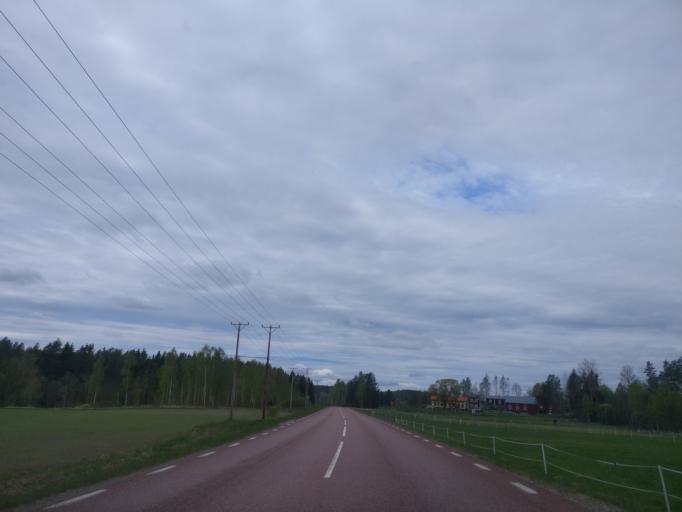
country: SE
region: Gaevleborg
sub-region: Soderhamns Kommun
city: Soderhamn
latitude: 61.3675
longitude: 16.9072
